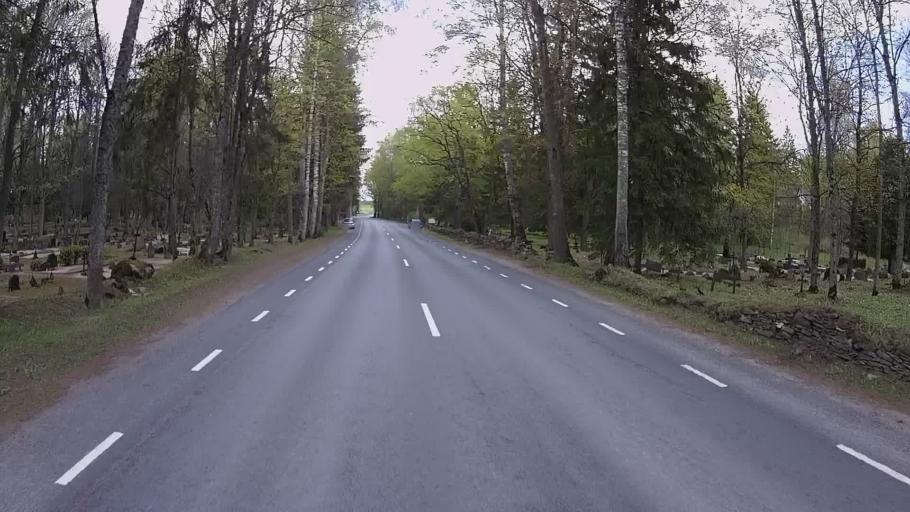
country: EE
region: Jaervamaa
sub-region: Koeru vald
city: Koeru
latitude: 58.9694
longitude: 26.0332
